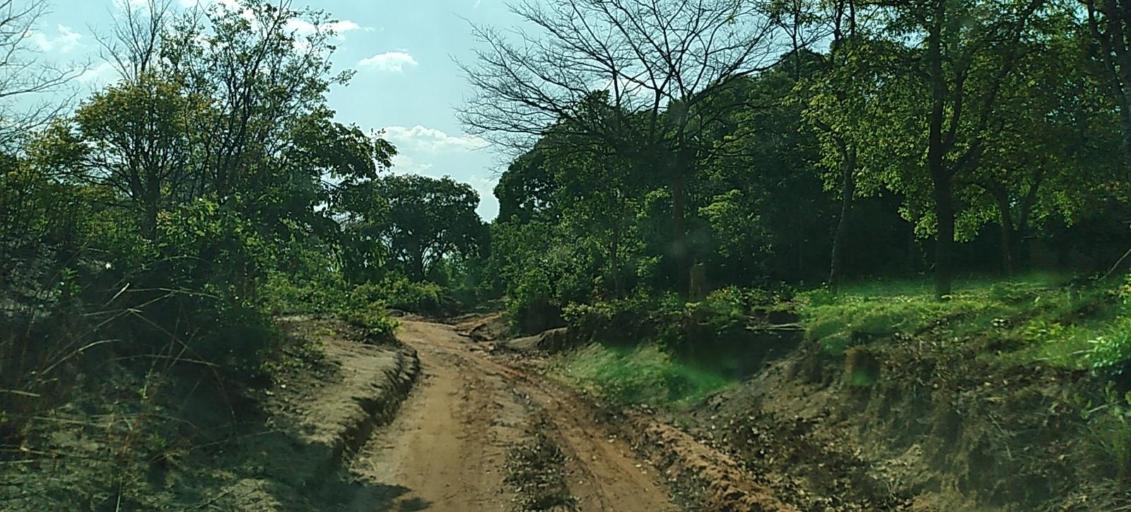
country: ZM
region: North-Western
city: Mwinilunga
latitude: -11.3005
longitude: 24.8716
